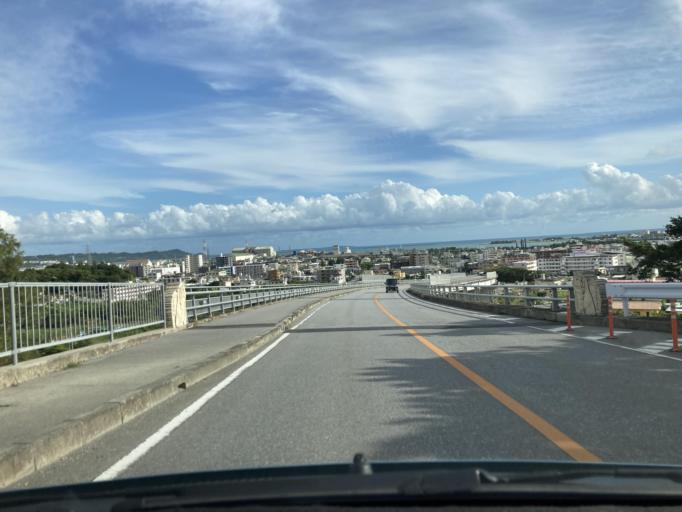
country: JP
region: Okinawa
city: Okinawa
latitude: 26.3397
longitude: 127.8334
